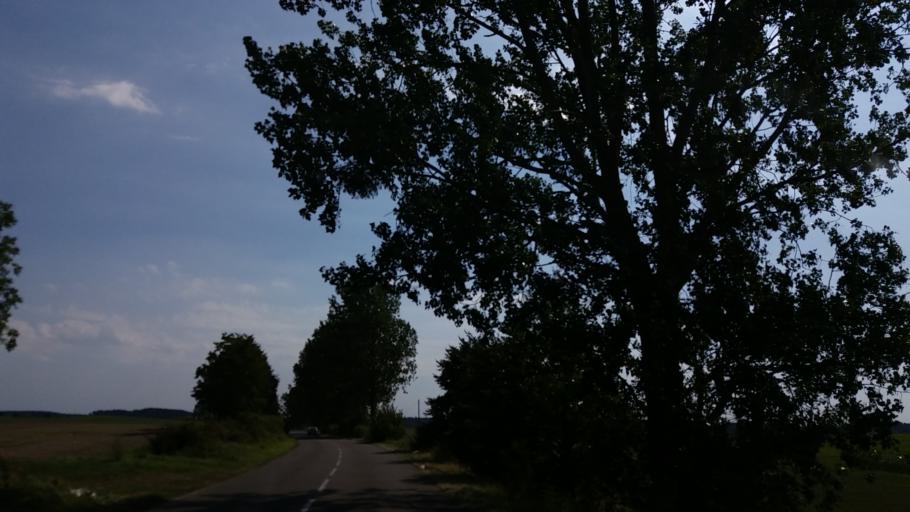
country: PL
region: West Pomeranian Voivodeship
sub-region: Powiat choszczenski
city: Krzecin
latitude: 53.1031
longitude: 15.4620
